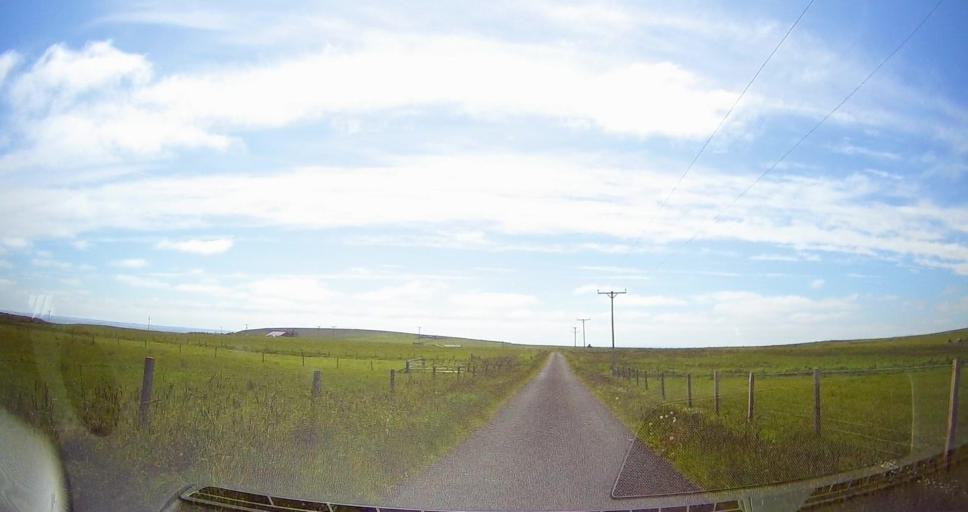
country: GB
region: Scotland
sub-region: Orkney Islands
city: Kirkwall
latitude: 58.8288
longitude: -2.8966
